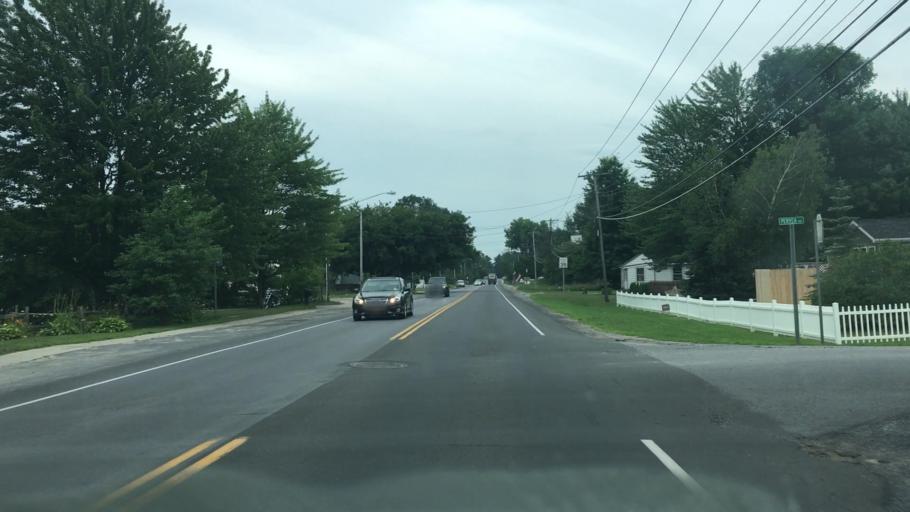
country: US
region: New York
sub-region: Clinton County
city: Plattsburgh West
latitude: 44.6822
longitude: -73.5065
